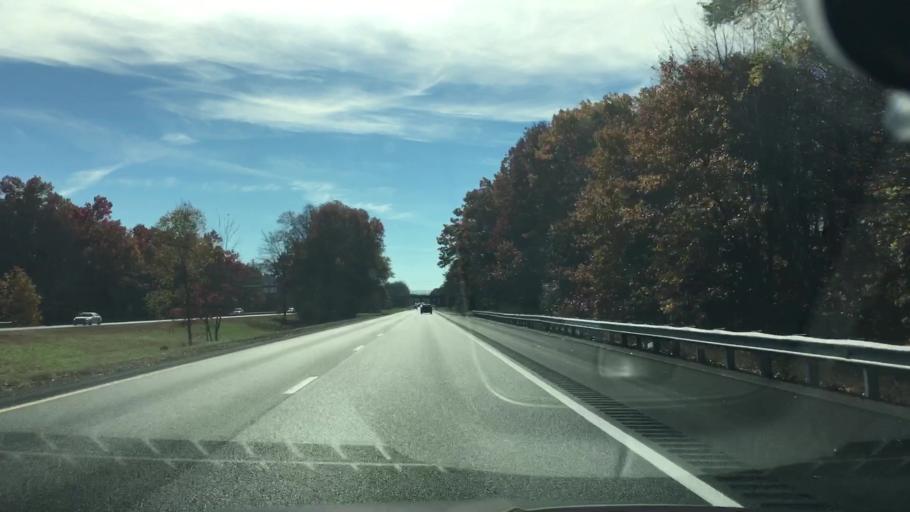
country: US
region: Massachusetts
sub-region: Hampshire County
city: Hatfield
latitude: 42.3864
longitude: -72.6308
